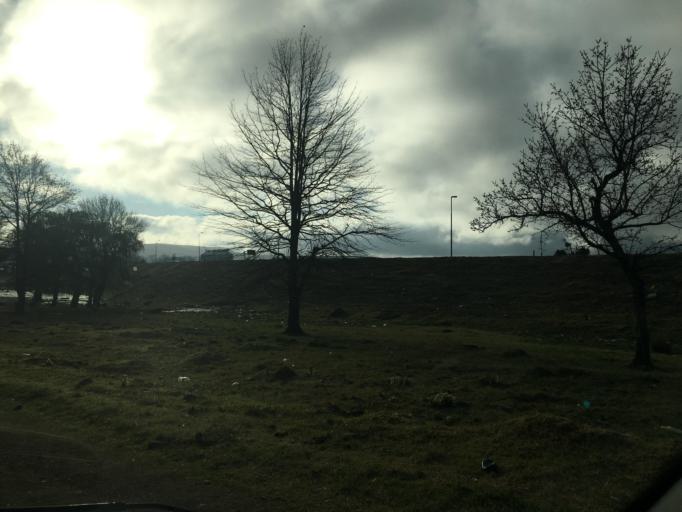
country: ZA
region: Eastern Cape
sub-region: Chris Hani District Municipality
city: Elliot
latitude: -31.3362
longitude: 27.8410
